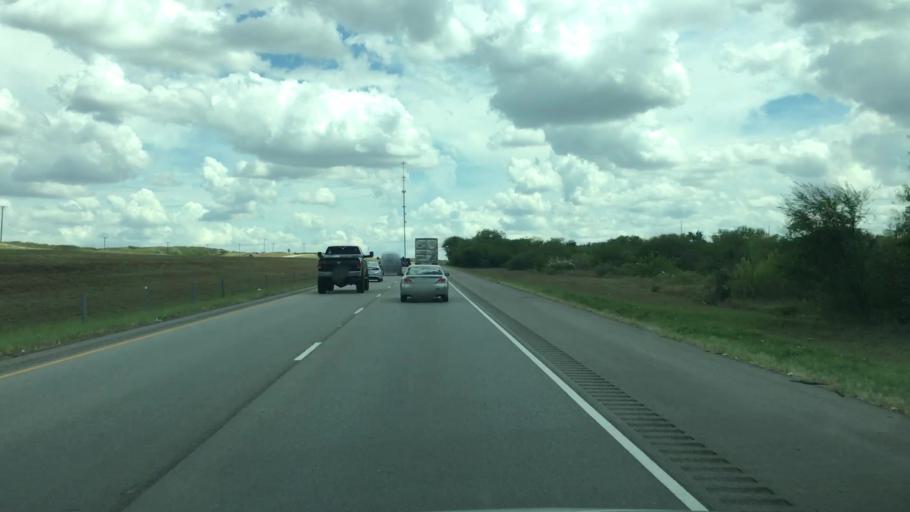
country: US
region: Texas
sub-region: San Patricio County
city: Mathis
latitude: 28.2601
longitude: -97.9285
